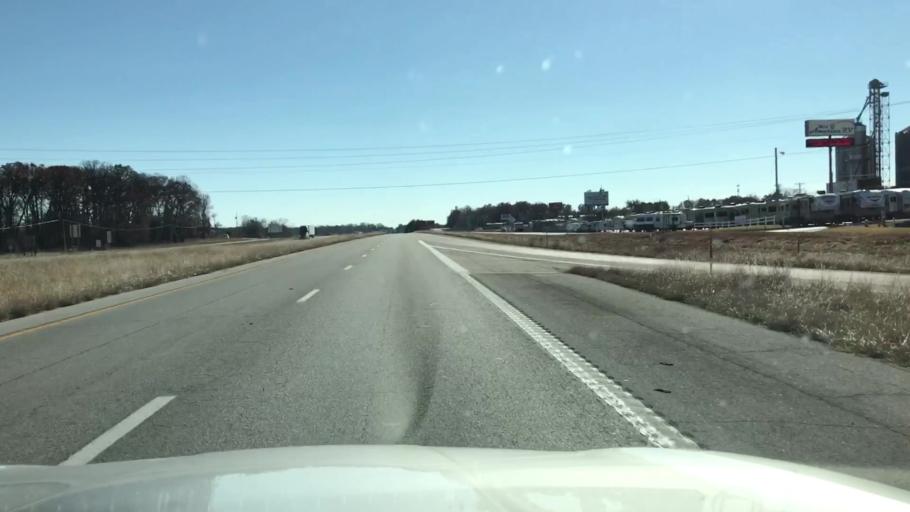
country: US
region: Missouri
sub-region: Jasper County
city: Carthage
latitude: 37.0938
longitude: -94.3124
